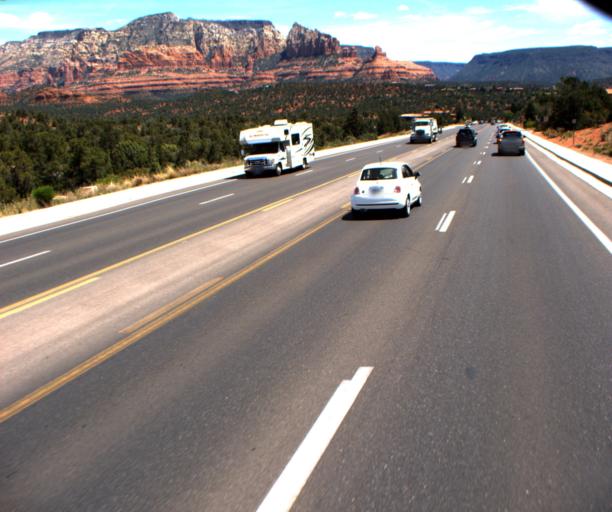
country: US
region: Arizona
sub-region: Coconino County
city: Sedona
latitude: 34.8633
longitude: -111.7784
